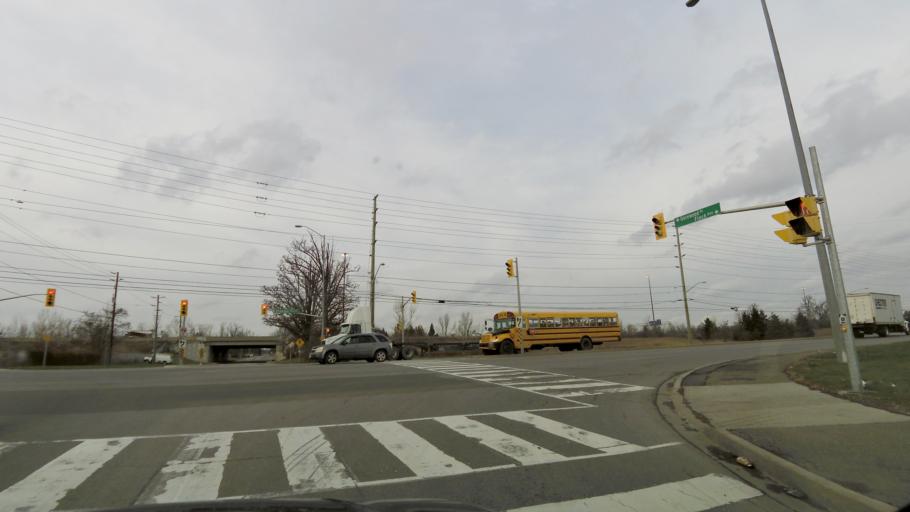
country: CA
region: Ontario
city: Etobicoke
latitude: 43.7426
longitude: -79.6470
